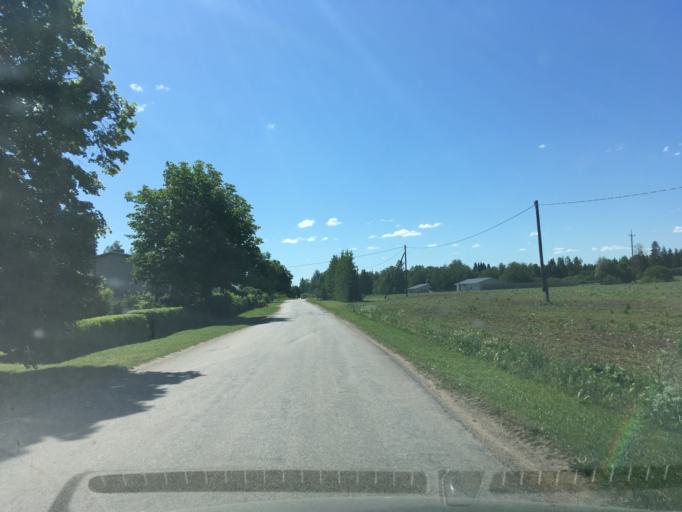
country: EE
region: Harju
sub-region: Rae vald
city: Vaida
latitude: 59.1663
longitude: 25.1246
